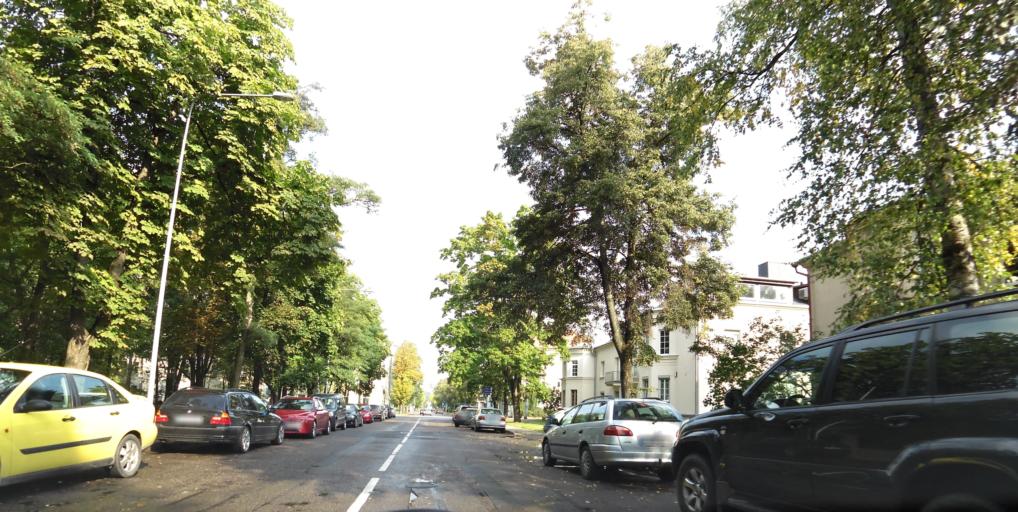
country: LT
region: Vilnius County
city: Naujamiestis
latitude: 54.6880
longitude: 25.2523
